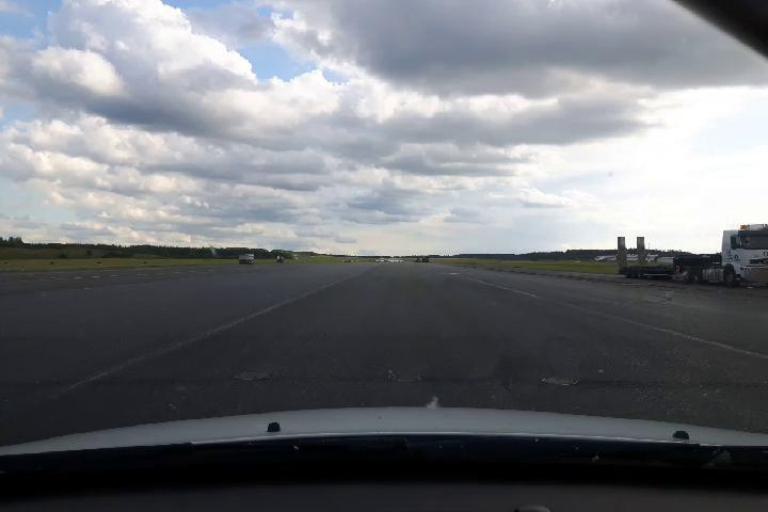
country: SE
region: Stockholm
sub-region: Sigtuna Kommun
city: Rosersberg
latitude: 59.6457
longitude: 17.9575
